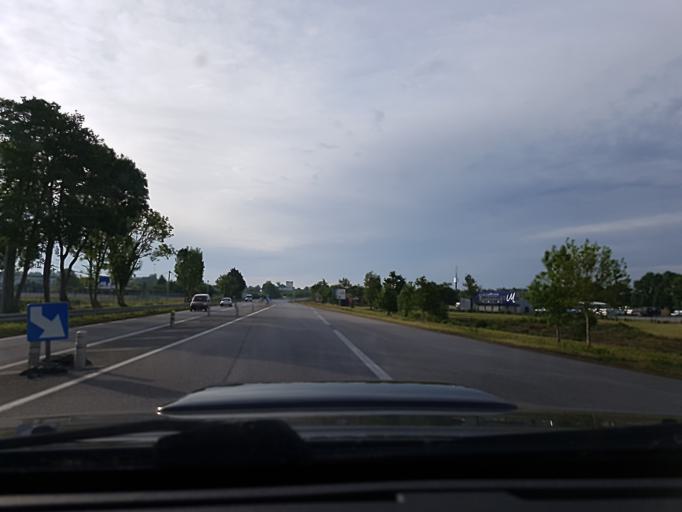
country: FR
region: Pays de la Loire
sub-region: Departement de la Vendee
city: Aizenay
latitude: 46.7508
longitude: -1.6291
